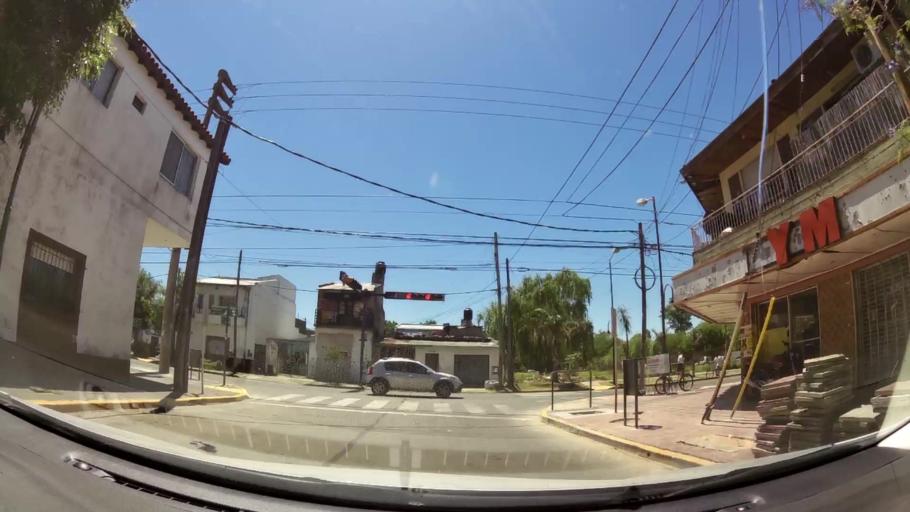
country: AR
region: Buenos Aires
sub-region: Partido de Tigre
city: Tigre
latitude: -34.4548
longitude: -58.5527
